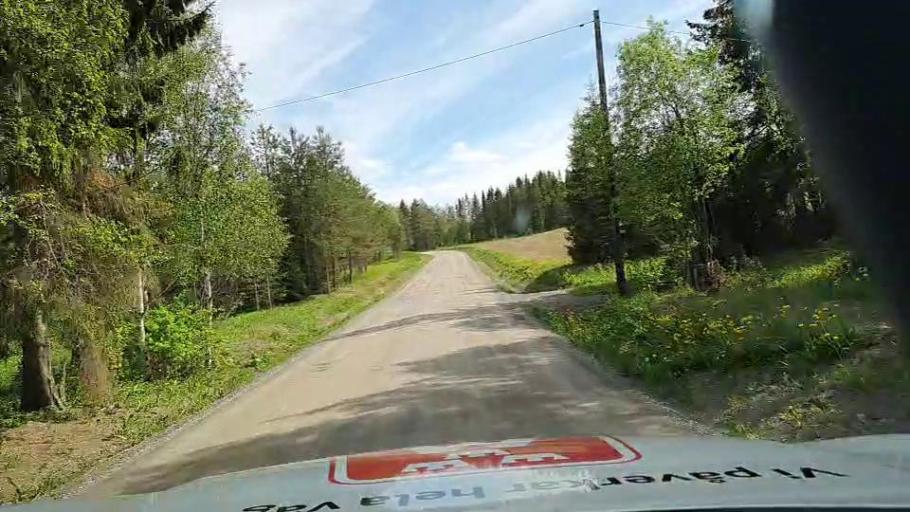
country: SE
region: Jaemtland
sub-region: OEstersunds Kommun
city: Brunflo
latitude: 63.0146
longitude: 14.7768
